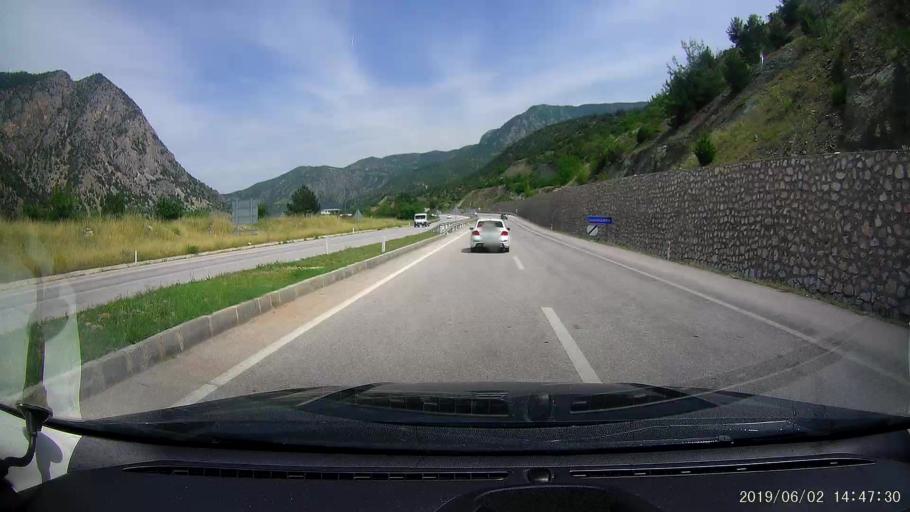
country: TR
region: Corum
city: Hacihamza
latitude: 41.0677
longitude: 34.4616
